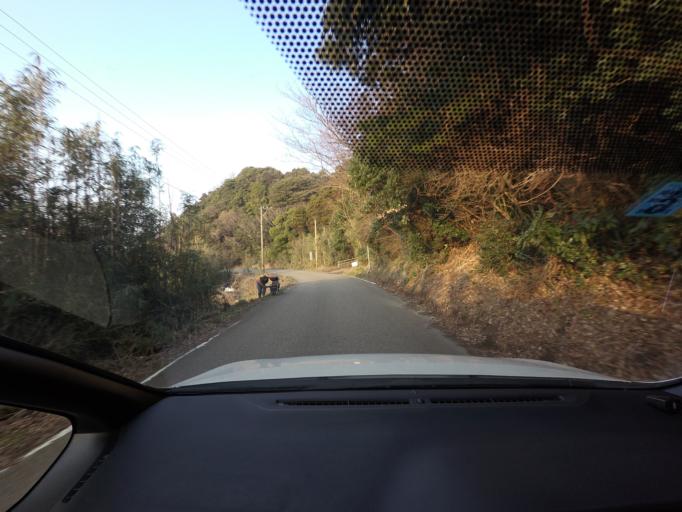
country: JP
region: Ishikawa
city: Nanao
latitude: 37.1637
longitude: 137.0323
